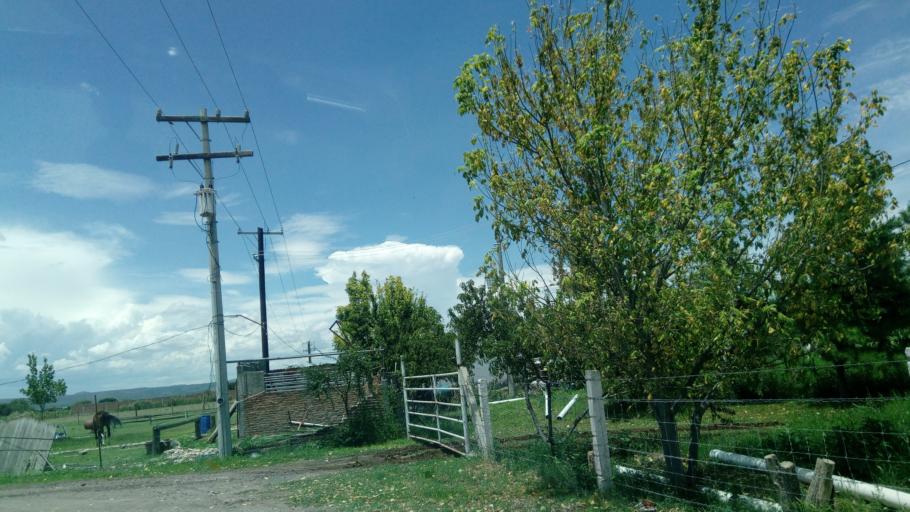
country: MX
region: Durango
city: Victoria de Durango
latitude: 24.0855
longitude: -104.5530
